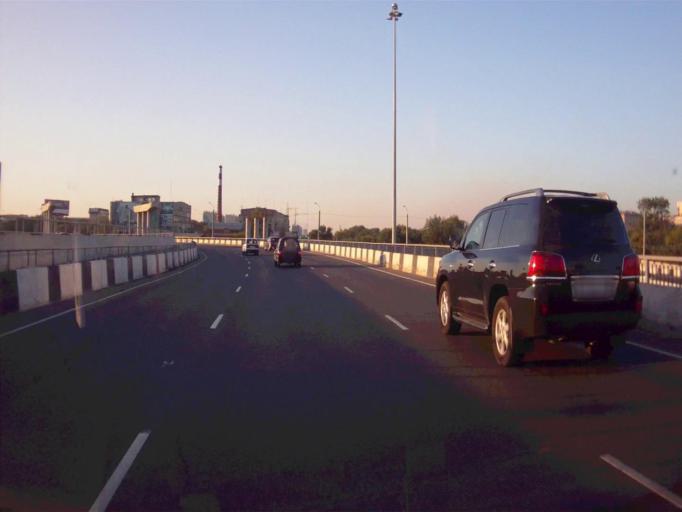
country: RU
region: Chelyabinsk
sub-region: Gorod Chelyabinsk
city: Chelyabinsk
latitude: 55.1712
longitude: 61.4139
